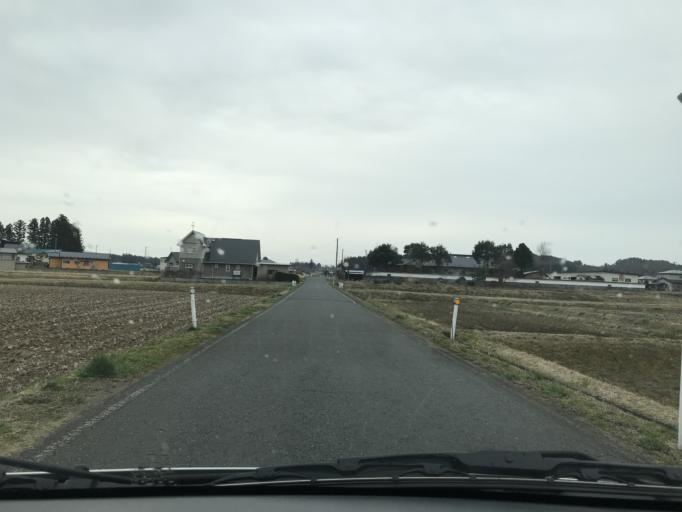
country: JP
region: Iwate
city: Mizusawa
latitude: 39.1286
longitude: 141.1085
